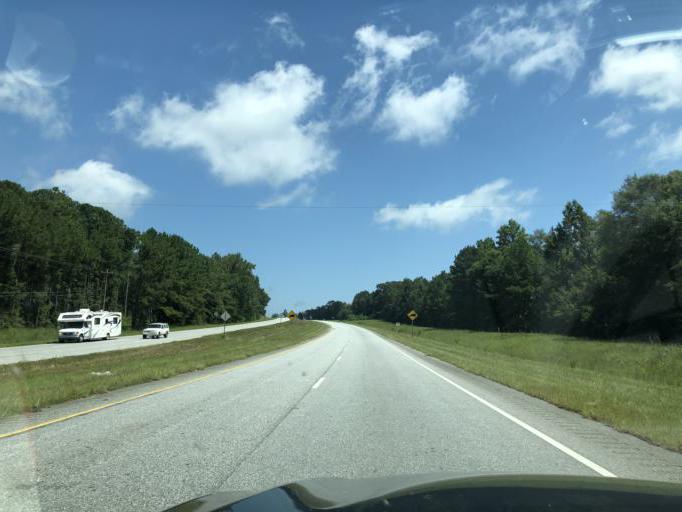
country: US
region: Alabama
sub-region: Barbour County
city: Eufaula
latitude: 31.7730
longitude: -85.1829
